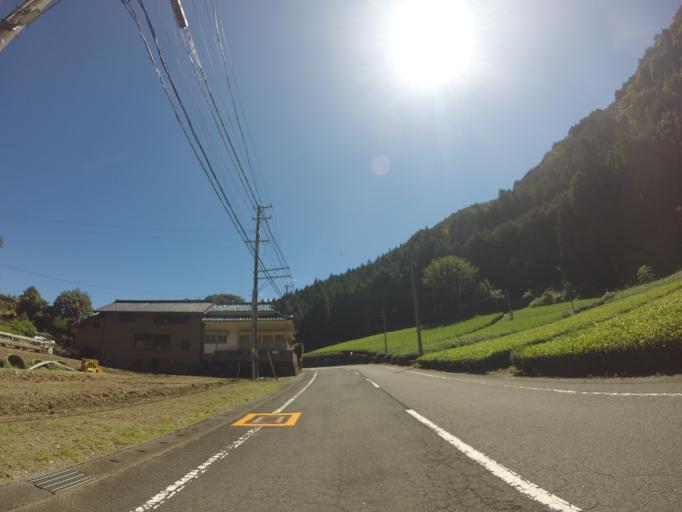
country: JP
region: Shizuoka
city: Fujieda
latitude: 34.9735
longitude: 138.1983
